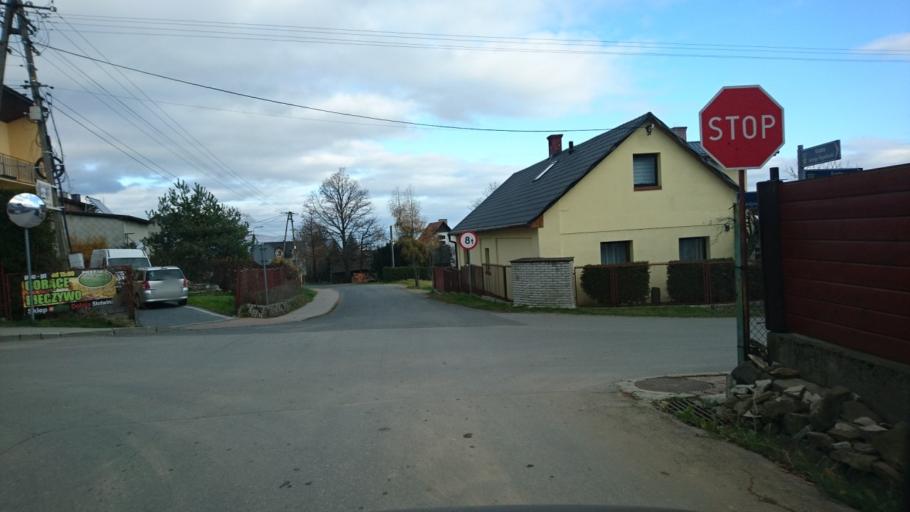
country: PL
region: Silesian Voivodeship
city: Godziszka
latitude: 49.7005
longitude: 19.0754
